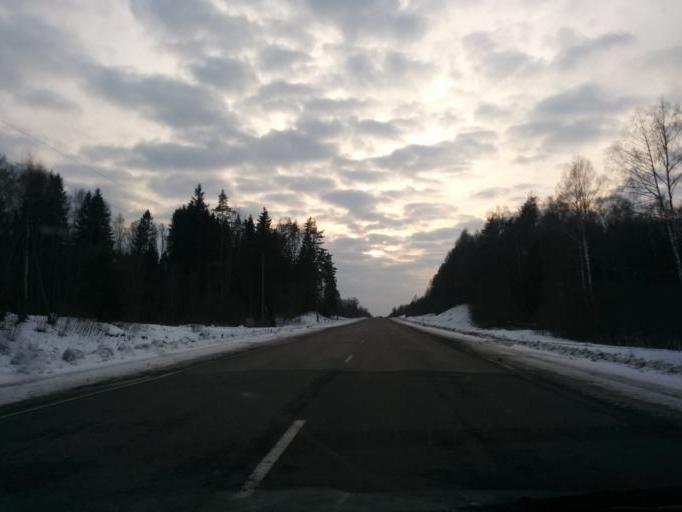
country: LV
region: Smiltene
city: Smiltene
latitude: 57.3271
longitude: 25.7960
